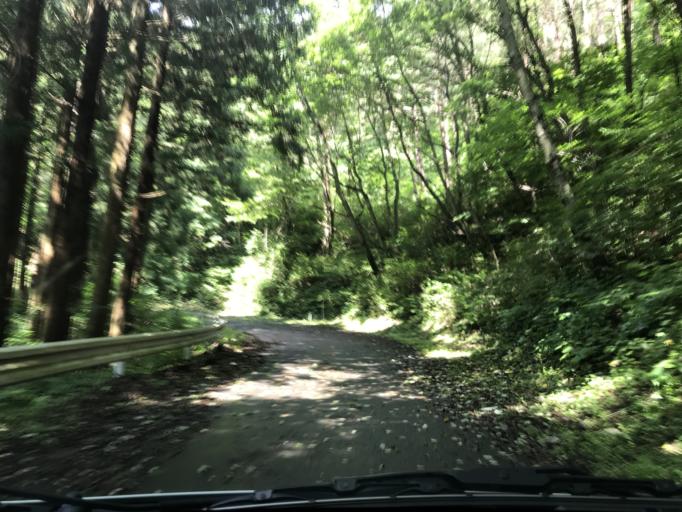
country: JP
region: Iwate
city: Ofunato
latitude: 38.9865
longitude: 141.4388
